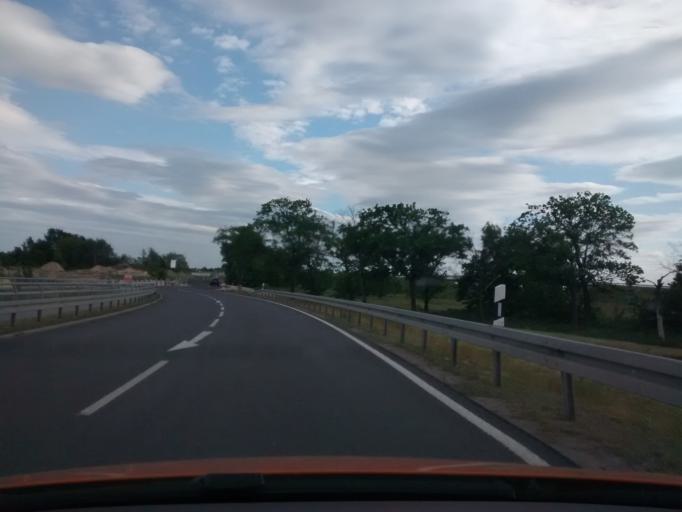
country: DE
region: Berlin
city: Bohnsdorf
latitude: 52.3713
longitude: 13.5498
